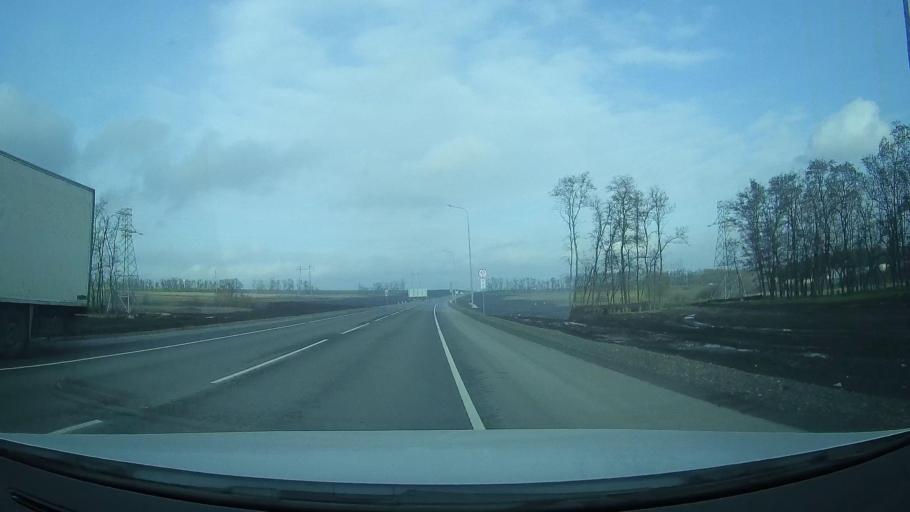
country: RU
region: Rostov
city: Grushevskaya
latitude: 47.3837
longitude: 39.8455
